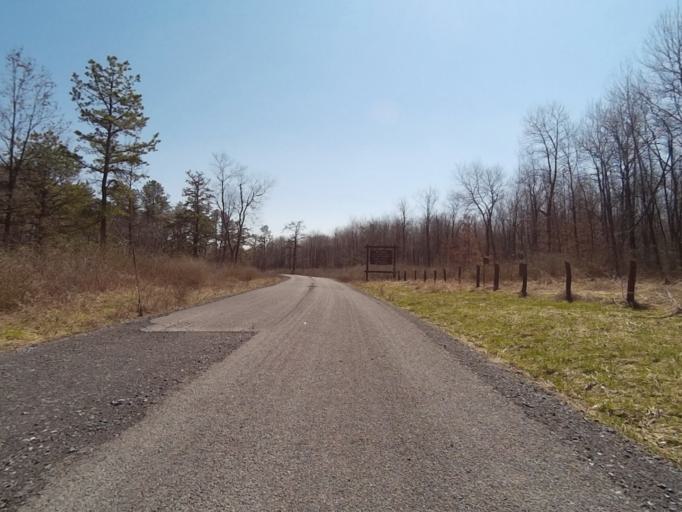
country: US
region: Pennsylvania
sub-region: Centre County
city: Park Forest Village
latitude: 40.7885
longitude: -77.9516
